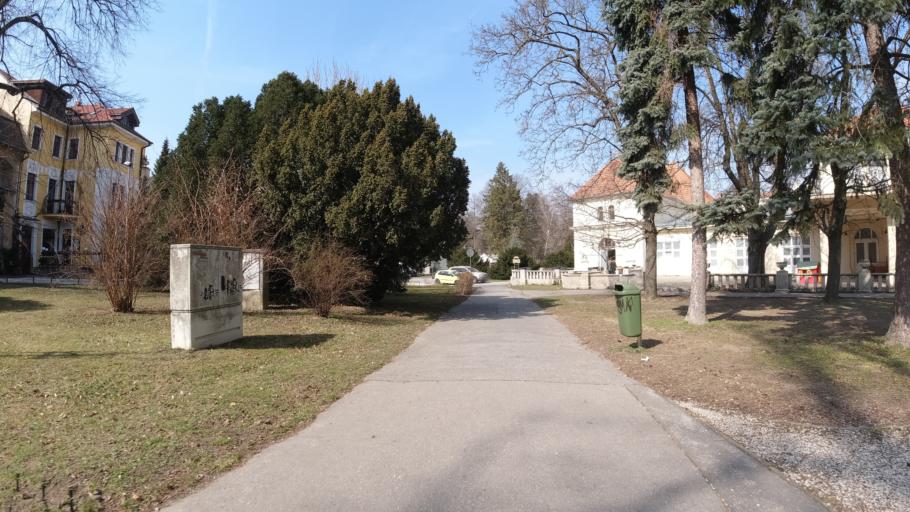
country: SK
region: Trnavsky
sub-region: Okres Trnava
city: Piestany
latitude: 48.5905
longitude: 17.8373
